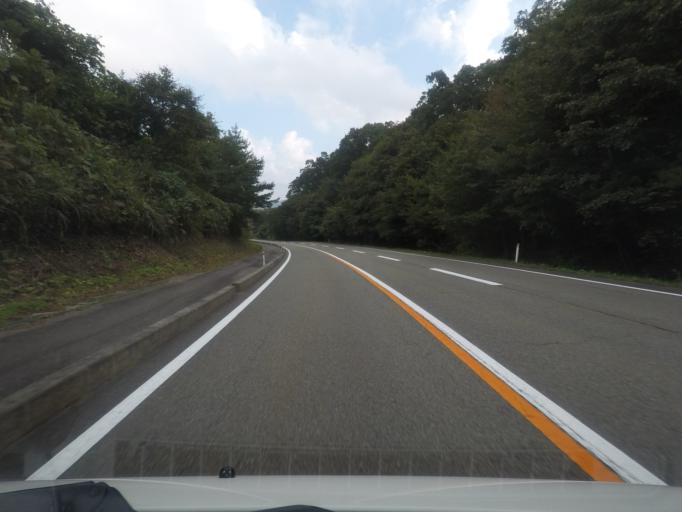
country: JP
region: Fukushima
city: Funehikimachi-funehiki
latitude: 37.5776
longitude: 140.7249
